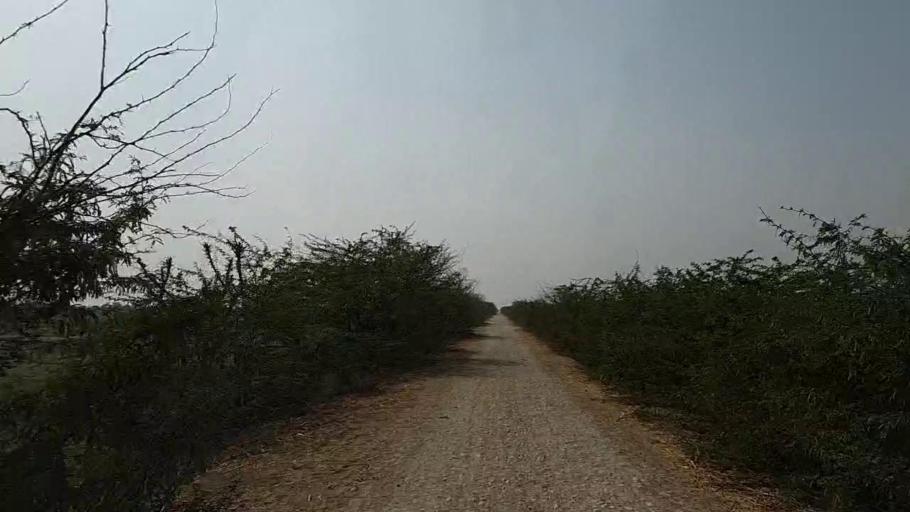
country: PK
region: Sindh
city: Naukot
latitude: 24.7605
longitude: 69.3372
